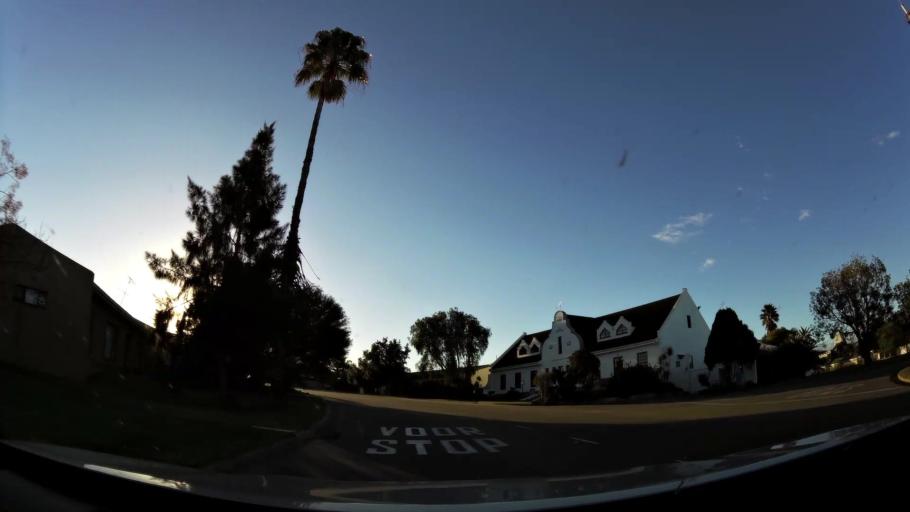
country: ZA
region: Western Cape
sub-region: Eden District Municipality
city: Riversdale
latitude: -34.0857
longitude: 21.2476
